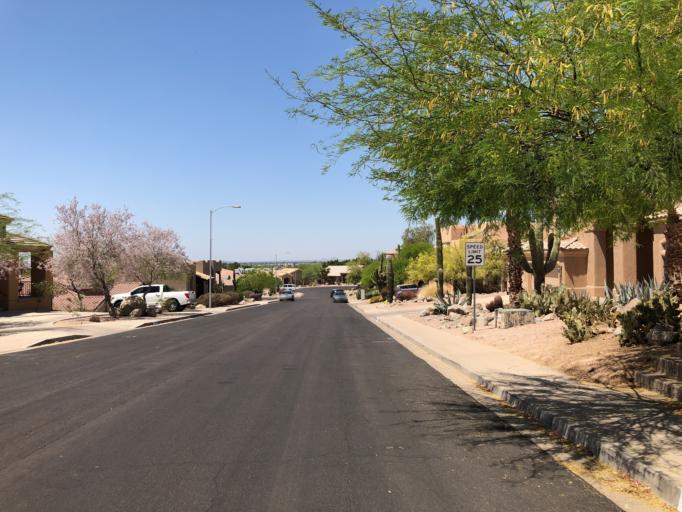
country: US
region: Arizona
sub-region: Maricopa County
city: Mesa
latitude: 33.4669
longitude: -111.6935
